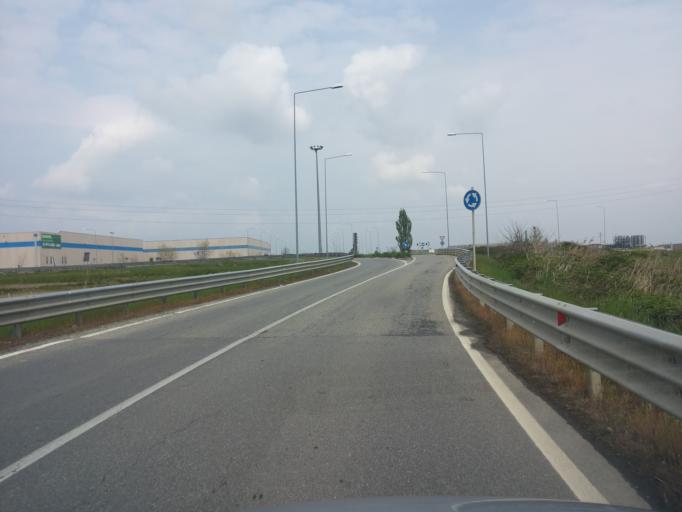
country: IT
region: Piedmont
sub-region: Provincia di Vercelli
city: Carisio
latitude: 45.4284
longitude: 8.2137
